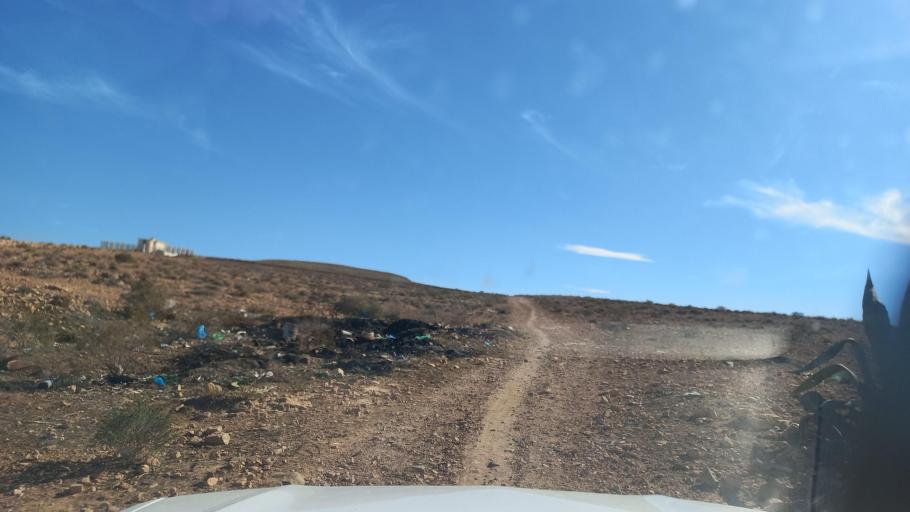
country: TN
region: Al Qasrayn
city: Kasserine
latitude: 35.2065
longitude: 8.9761
